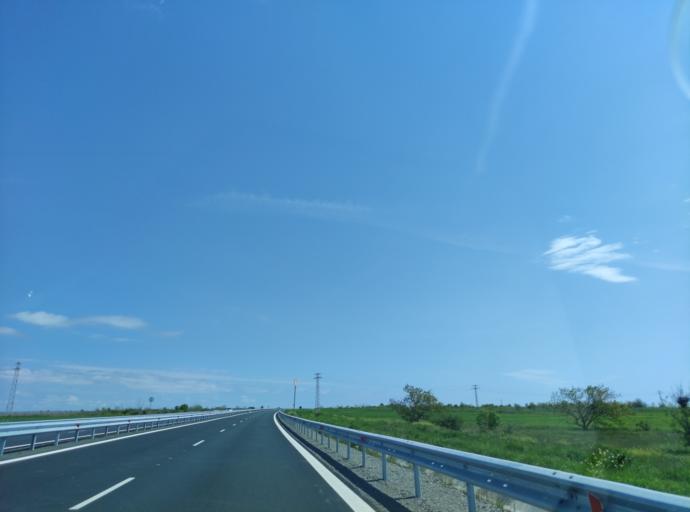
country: BG
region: Burgas
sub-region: Obshtina Pomorie
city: Pomorie
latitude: 42.5805
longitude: 27.5815
